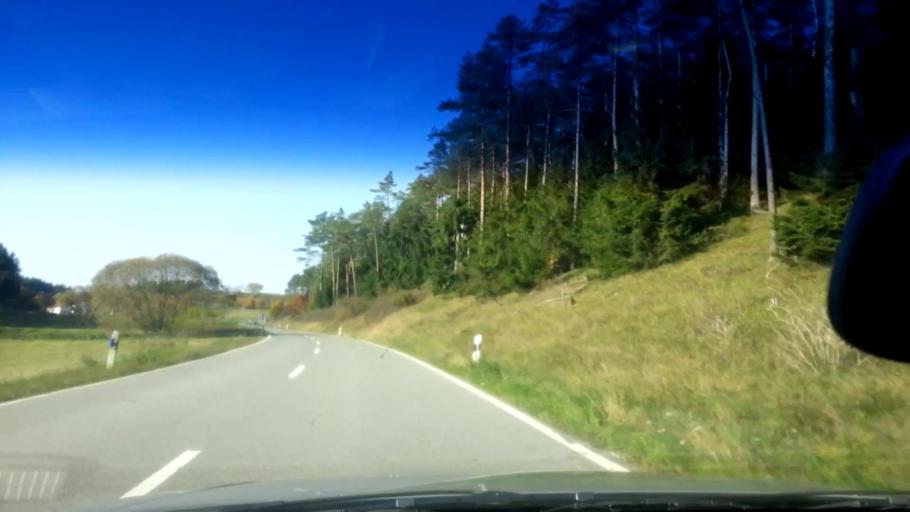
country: DE
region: Bavaria
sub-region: Upper Franconia
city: Stadelhofen
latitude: 49.9745
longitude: 11.1882
